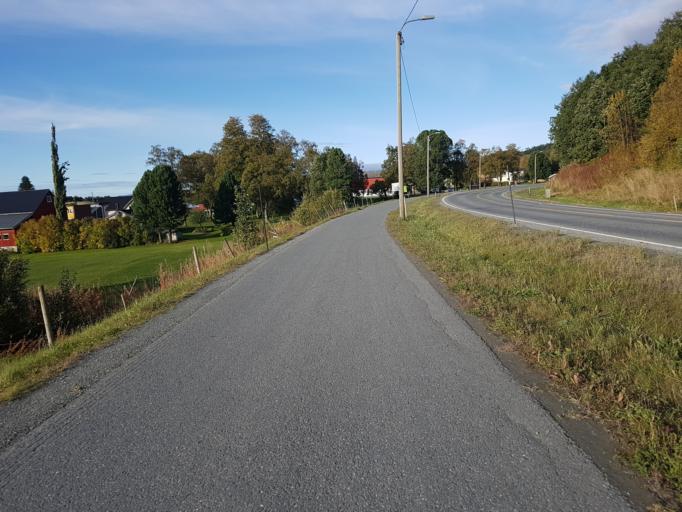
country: NO
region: Sor-Trondelag
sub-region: Trondheim
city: Trondheim
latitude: 63.3749
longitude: 10.4299
